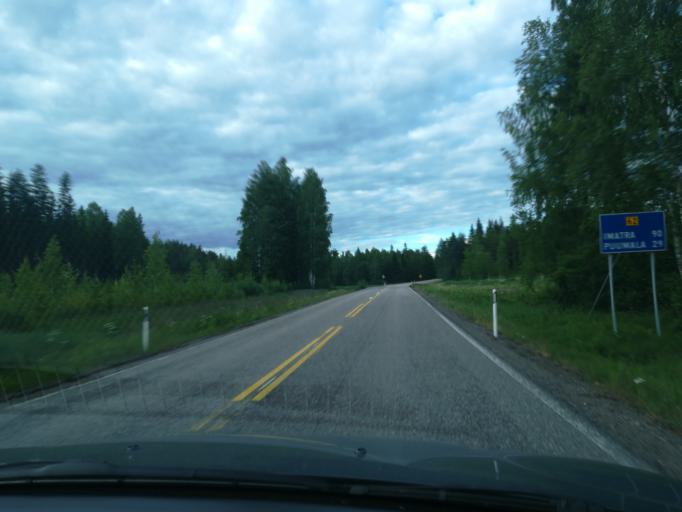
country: FI
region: Southern Savonia
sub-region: Mikkeli
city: Puumala
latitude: 61.5083
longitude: 27.8709
